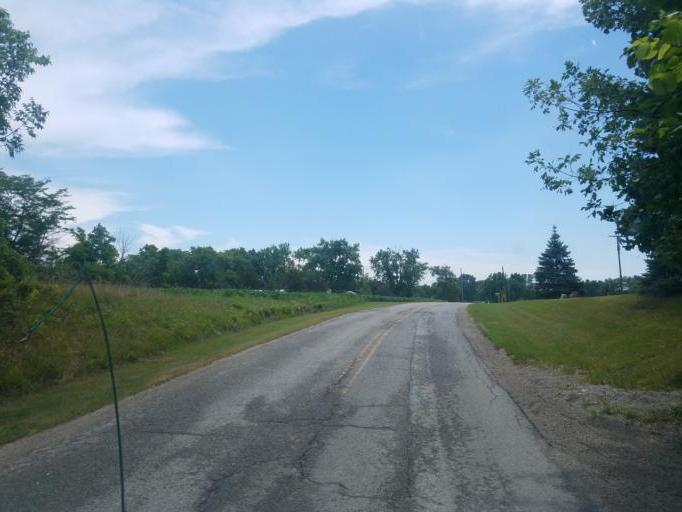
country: US
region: Ohio
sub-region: Paulding County
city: Antwerp
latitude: 41.2001
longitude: -84.7275
